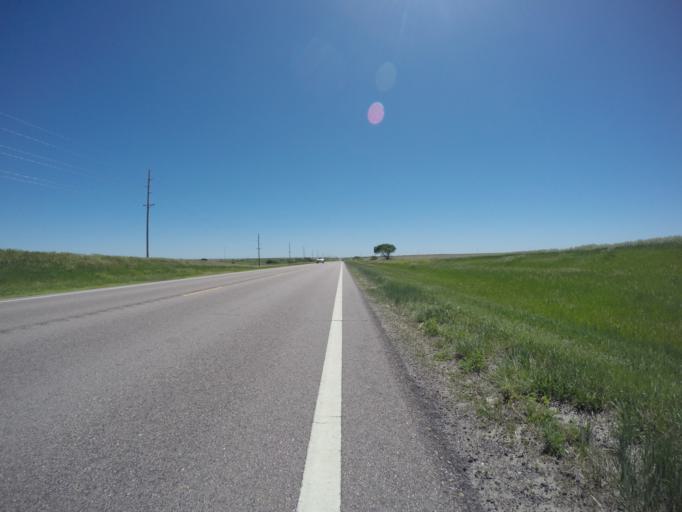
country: US
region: Kansas
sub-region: Norton County
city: Norton
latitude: 39.8284
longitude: -99.6321
